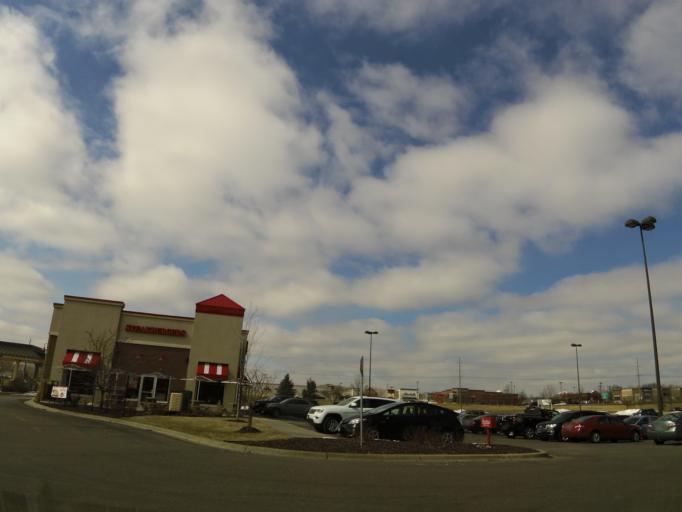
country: US
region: Minnesota
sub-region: Scott County
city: Savage
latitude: 44.7473
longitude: -93.3779
